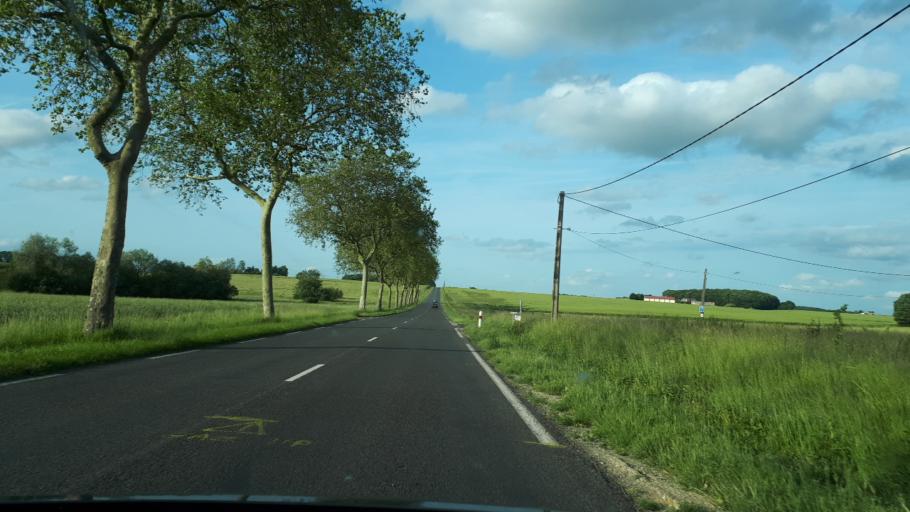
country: FR
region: Centre
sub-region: Departement d'Indre-et-Loire
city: Monnaie
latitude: 47.5155
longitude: 0.8123
